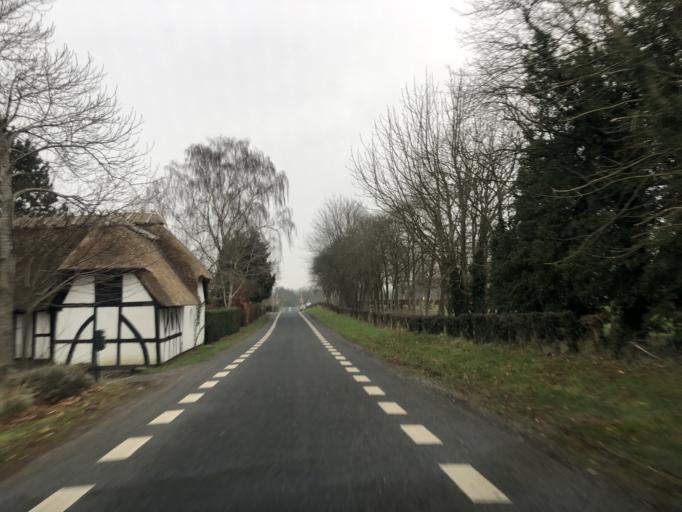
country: DK
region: South Denmark
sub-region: Faaborg-Midtfyn Kommune
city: Arslev
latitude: 55.2981
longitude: 10.4675
